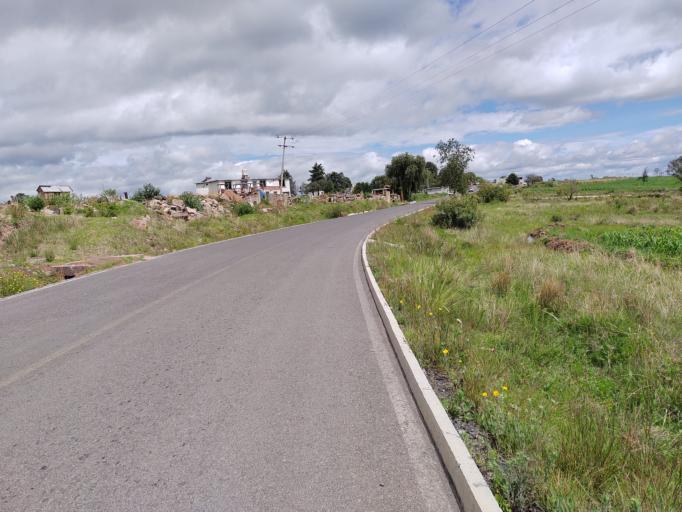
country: MX
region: Mexico
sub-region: Aculco
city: Gunyo Poniente (San Jose Gunyo)
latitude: 20.1139
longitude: -99.8715
